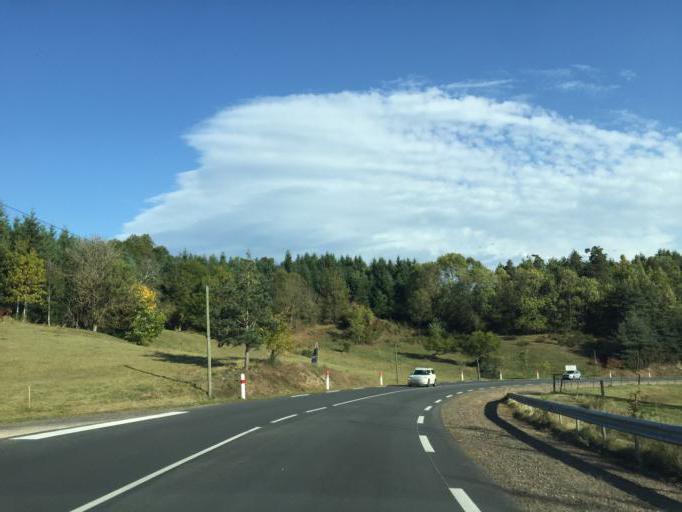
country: FR
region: Rhone-Alpes
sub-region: Departement de la Loire
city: Saint-Bonnet-le-Chateau
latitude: 45.4415
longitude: 4.0656
